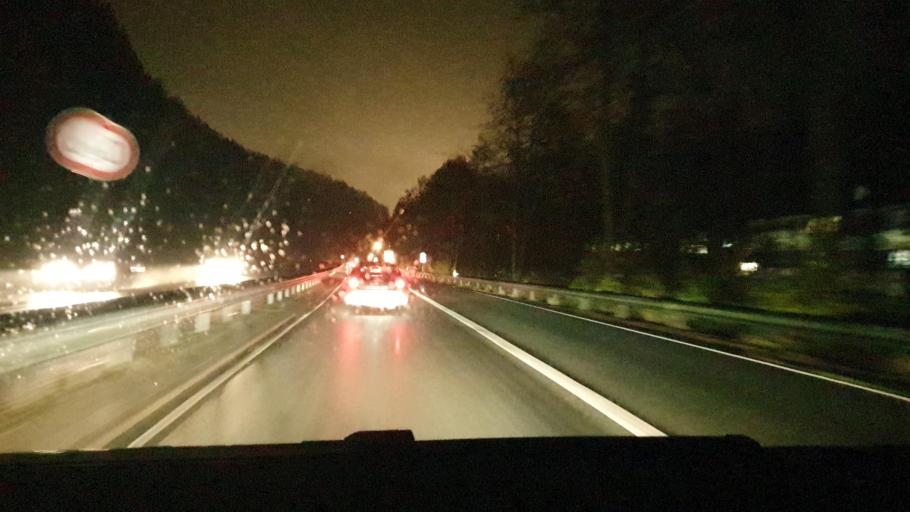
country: DE
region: North Rhine-Westphalia
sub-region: Regierungsbezirk Arnsberg
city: Siegen
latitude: 50.8859
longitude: 7.9992
